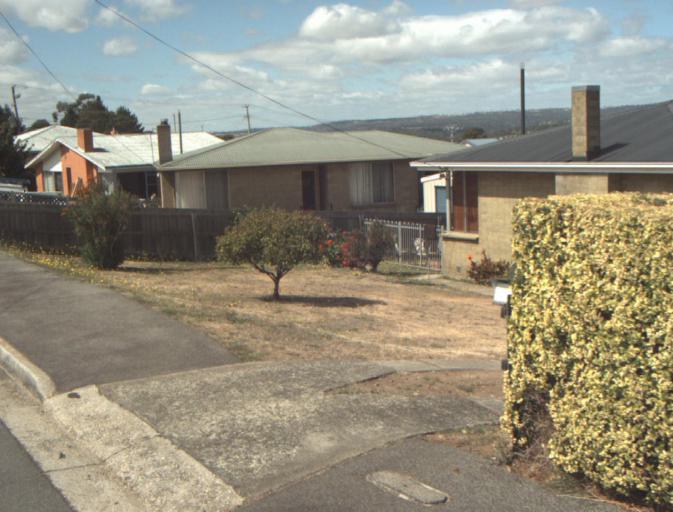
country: AU
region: Tasmania
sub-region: Launceston
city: Newstead
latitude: -41.4214
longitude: 147.1734
